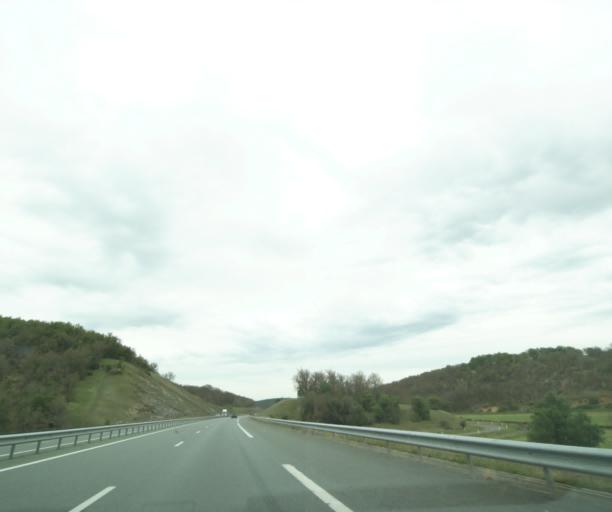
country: FR
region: Midi-Pyrenees
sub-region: Departement du Lot
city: Le Vigan
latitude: 44.7561
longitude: 1.5398
